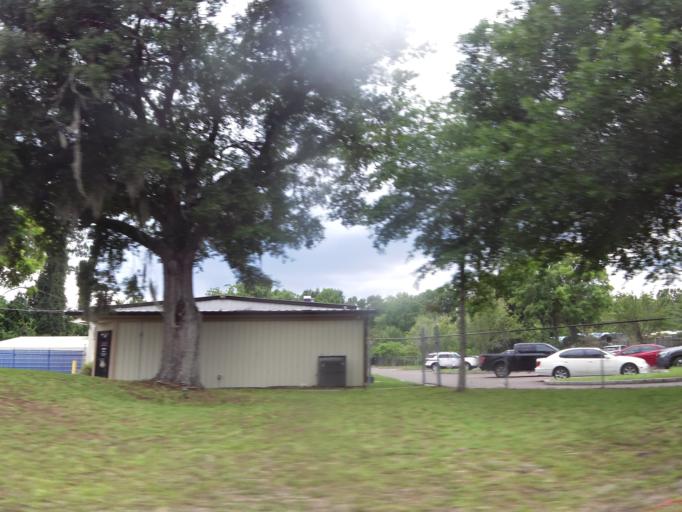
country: US
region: Florida
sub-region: Duval County
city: Jacksonville
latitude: 30.3244
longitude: -81.5360
